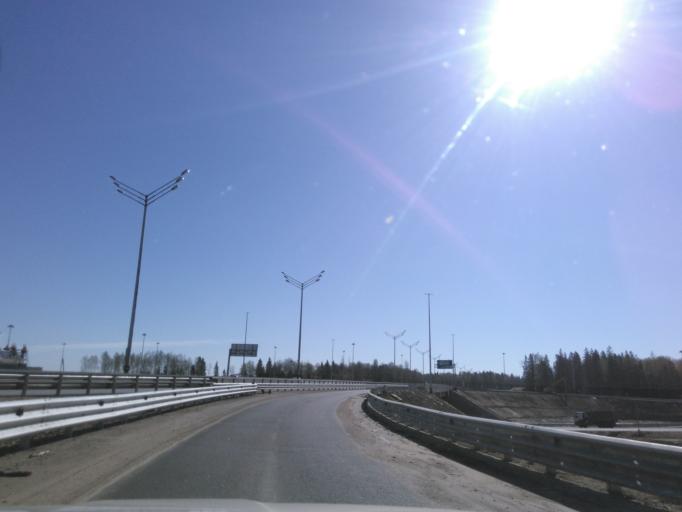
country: RU
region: Moskovskaya
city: Radumlya
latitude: 56.0986
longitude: 37.1724
